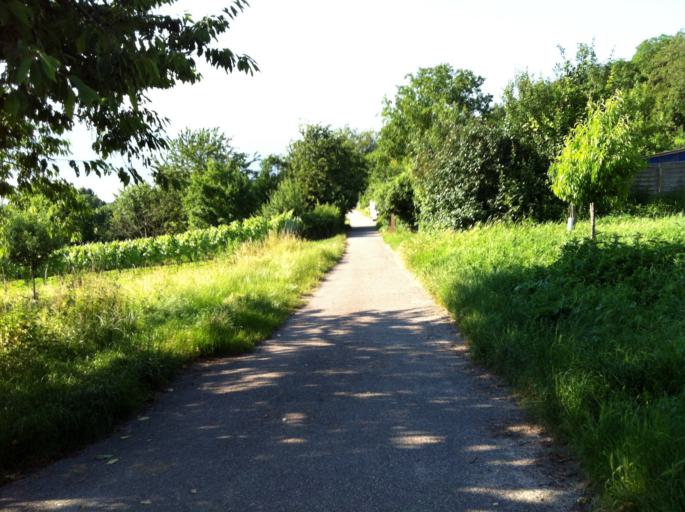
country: DE
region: Baden-Wuerttemberg
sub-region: Karlsruhe Region
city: Leimen
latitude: 49.3713
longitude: 8.6945
